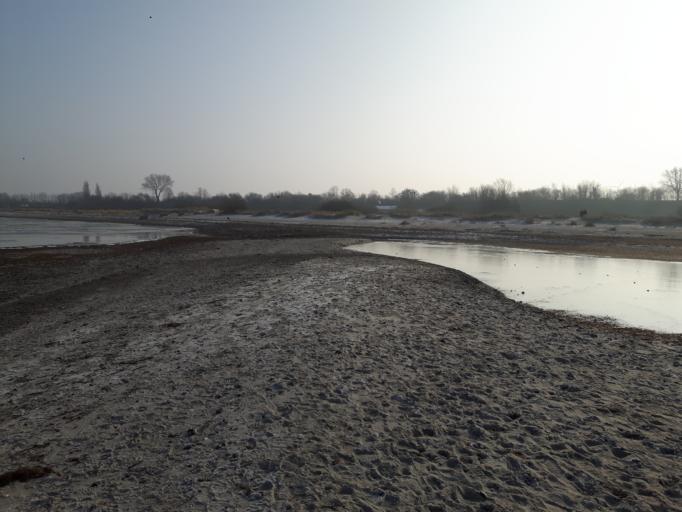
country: DE
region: Schleswig-Holstein
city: Laboe
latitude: 54.4157
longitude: 10.2325
